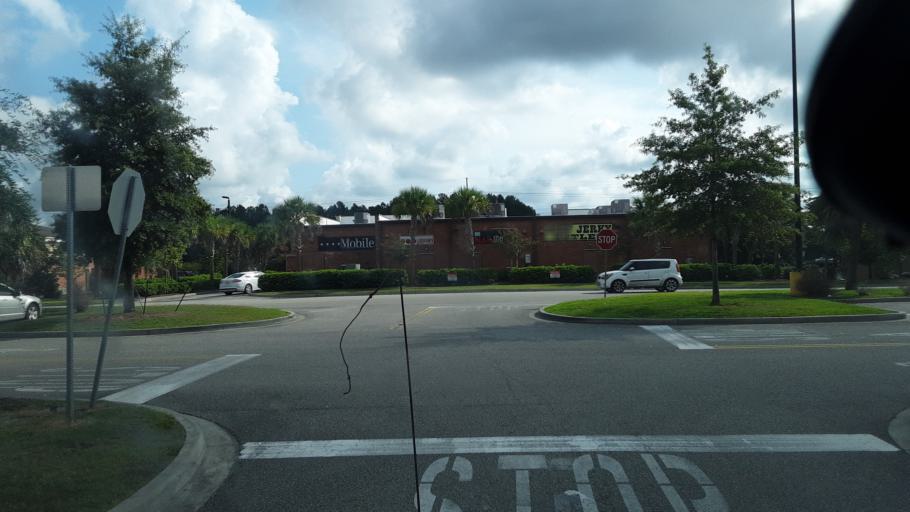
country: US
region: South Carolina
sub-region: Horry County
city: Red Hill
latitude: 33.7782
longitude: -78.9883
